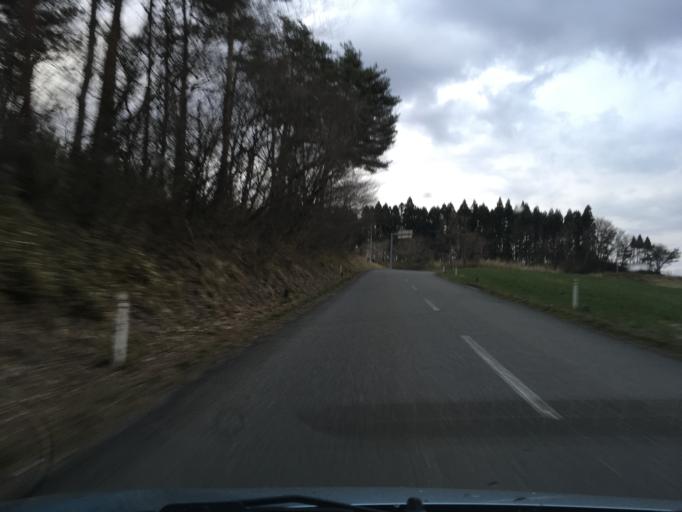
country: JP
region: Iwate
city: Ichinoseki
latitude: 38.7798
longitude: 141.2444
